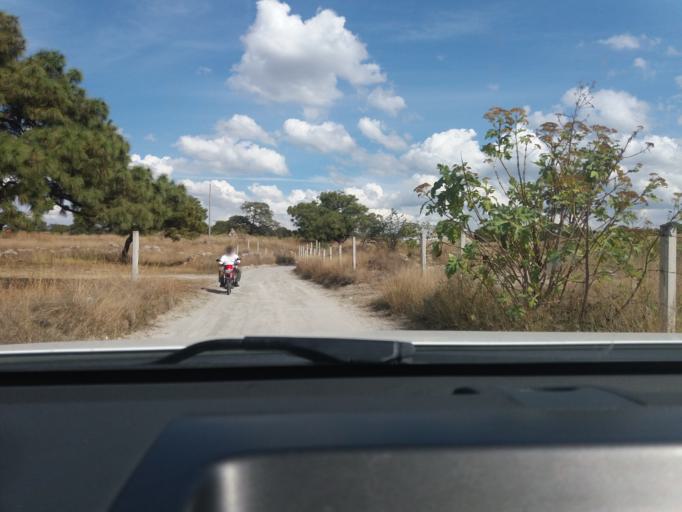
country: MX
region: Jalisco
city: Tala
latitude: 20.6577
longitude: -103.6836
